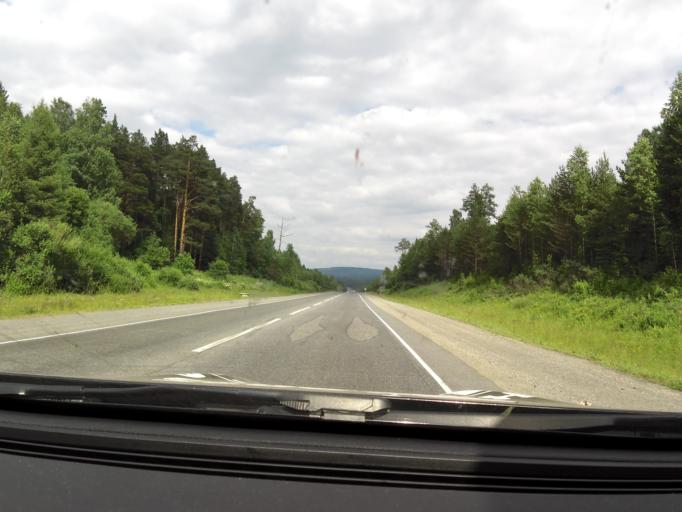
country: RU
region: Sverdlovsk
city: Druzhinino
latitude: 56.8279
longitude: 59.5981
